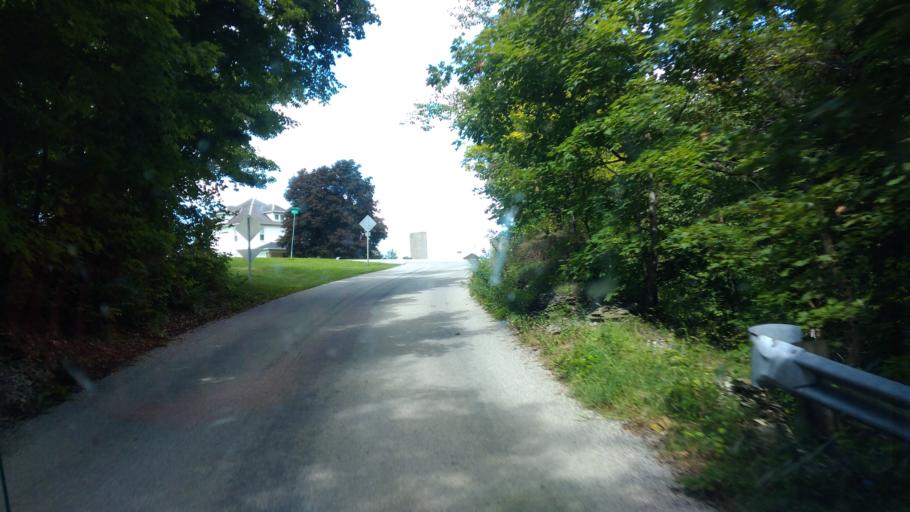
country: US
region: Ohio
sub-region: Huron County
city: Monroeville
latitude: 41.2815
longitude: -82.6782
